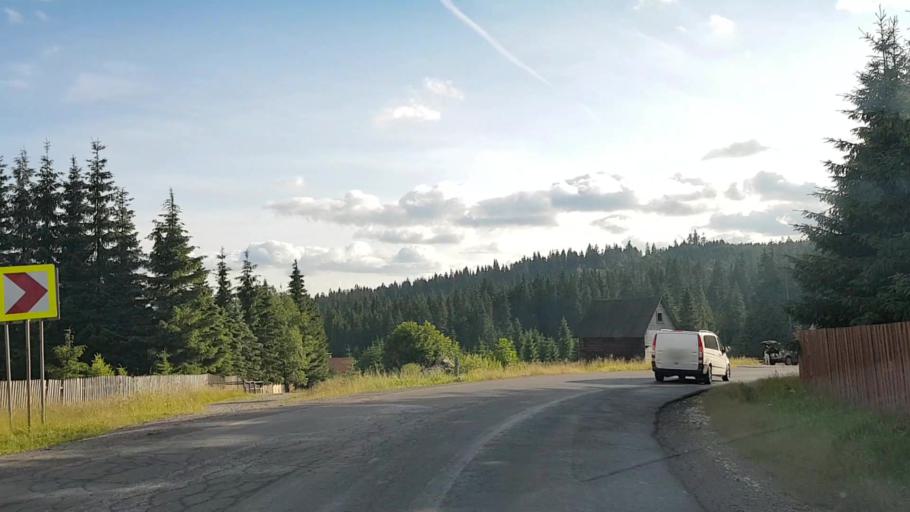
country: RO
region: Harghita
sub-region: Comuna Varsag
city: Varsag
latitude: 46.6553
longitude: 25.2960
